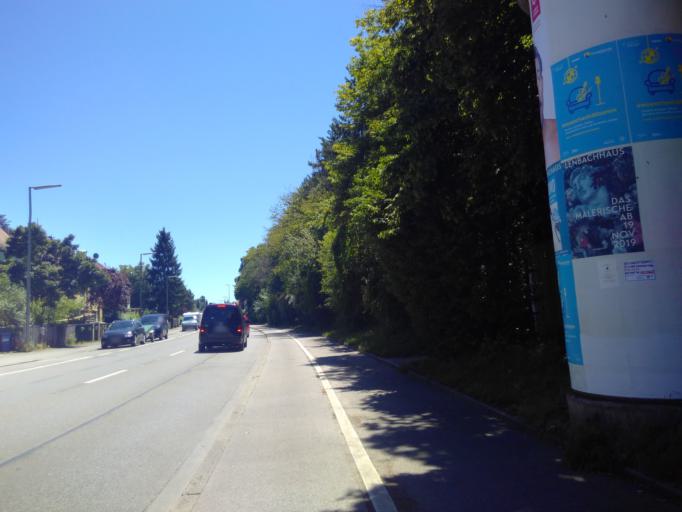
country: DE
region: Bavaria
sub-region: Upper Bavaria
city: Pasing
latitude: 48.1315
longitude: 11.4827
